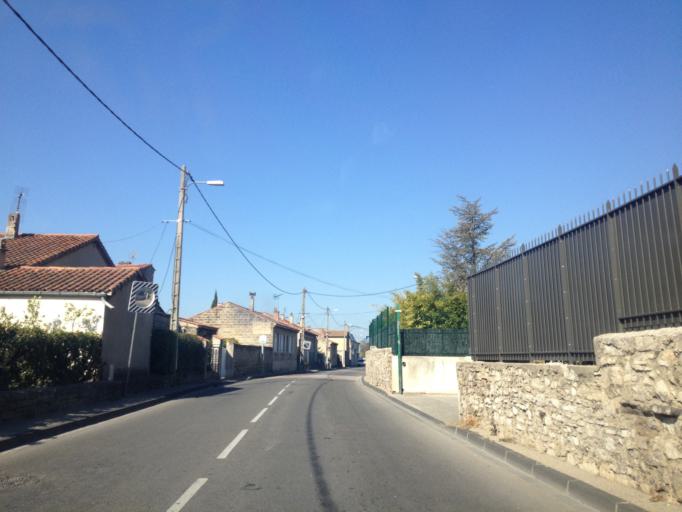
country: FR
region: Provence-Alpes-Cote d'Azur
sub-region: Departement du Vaucluse
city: Carpentras
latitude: 44.0610
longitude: 5.0535
